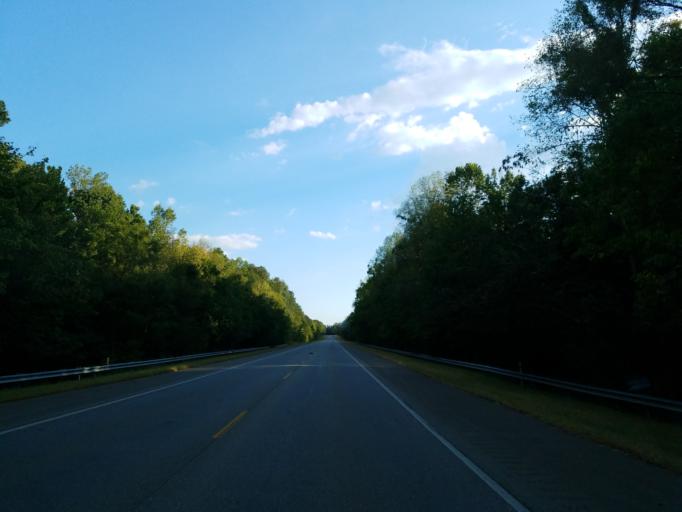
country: US
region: Georgia
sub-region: Murray County
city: Chatsworth
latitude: 34.6630
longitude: -84.7209
